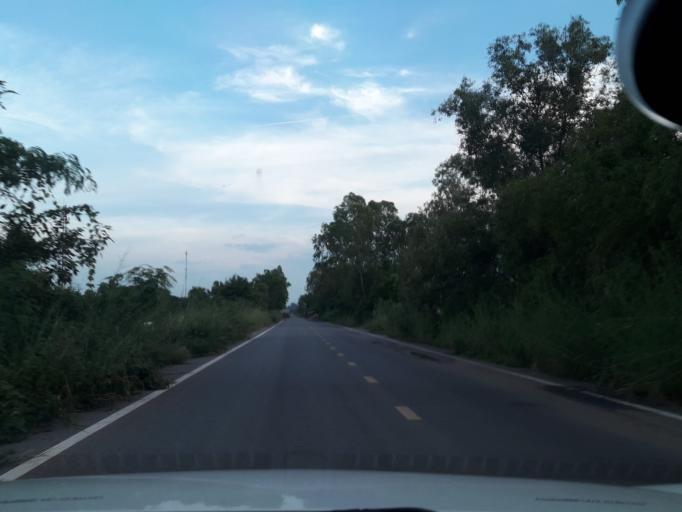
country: TH
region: Sara Buri
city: Nong Khae
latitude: 14.3095
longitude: 100.8860
